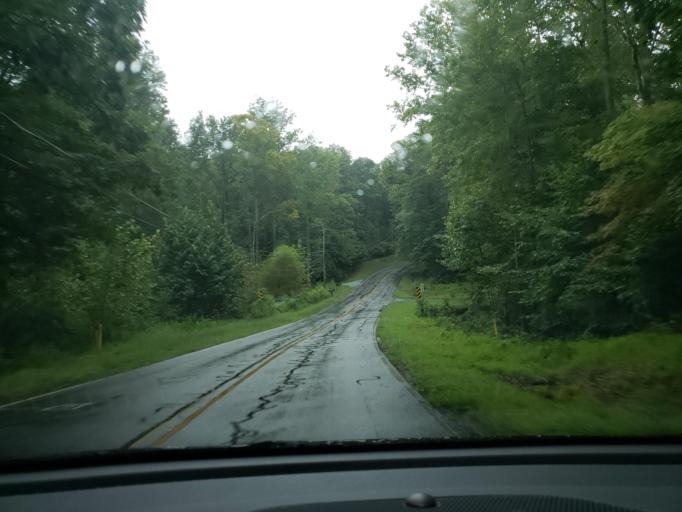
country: US
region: North Carolina
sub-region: Orange County
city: Chapel Hill
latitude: 35.9924
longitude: -79.0030
